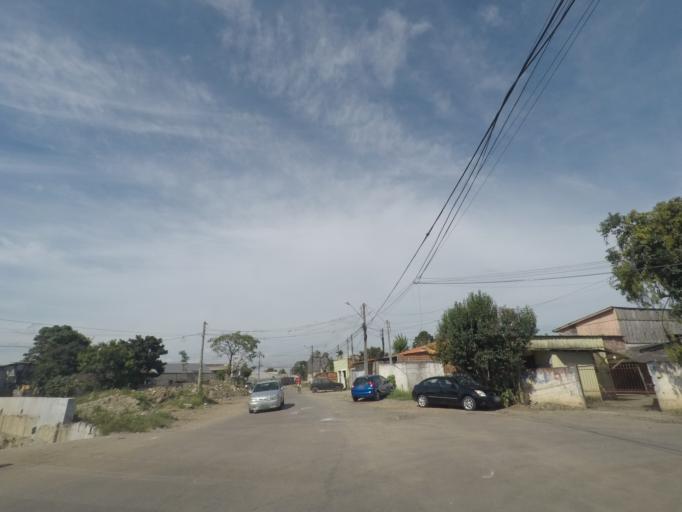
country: BR
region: Parana
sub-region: Curitiba
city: Curitiba
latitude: -25.4671
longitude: -49.2625
